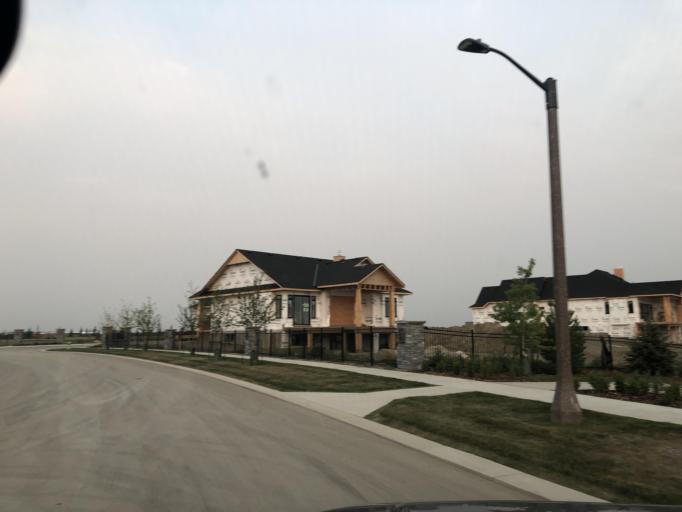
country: CA
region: Alberta
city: Cochrane
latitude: 51.1191
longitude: -114.3939
